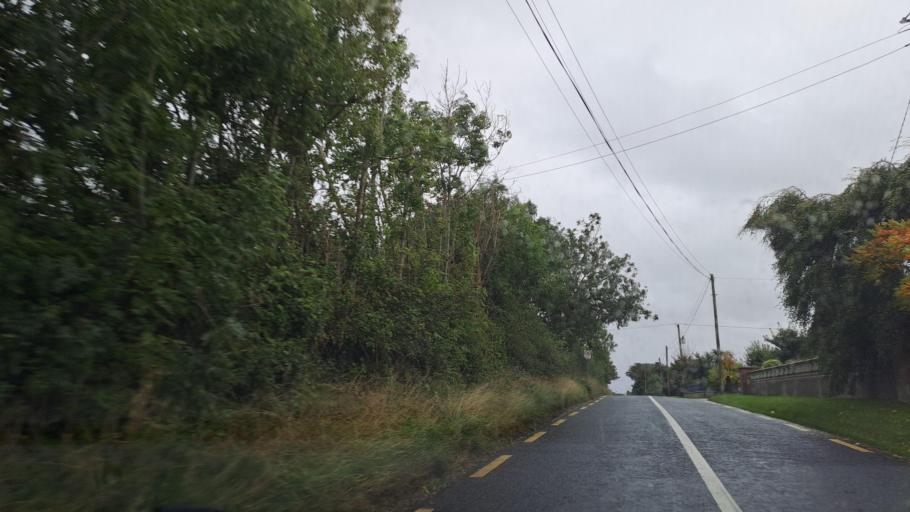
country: IE
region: Leinster
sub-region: Lu
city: Dromiskin
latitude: 53.9597
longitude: -6.4521
